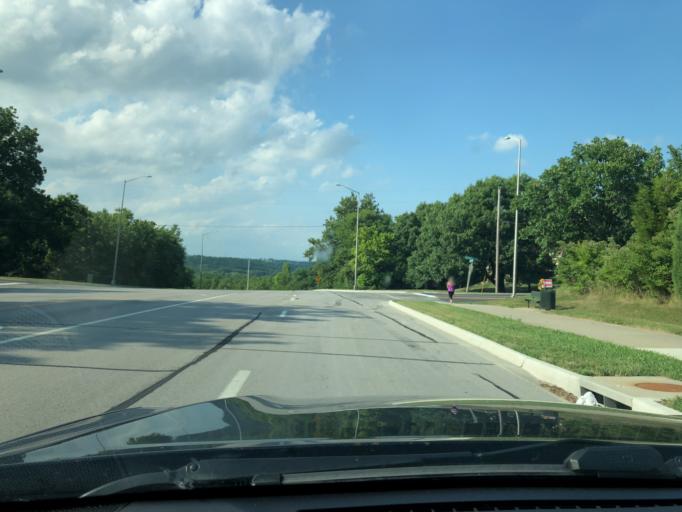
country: US
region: Kansas
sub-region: Leavenworth County
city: Leavenworth
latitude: 39.3005
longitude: -94.9525
